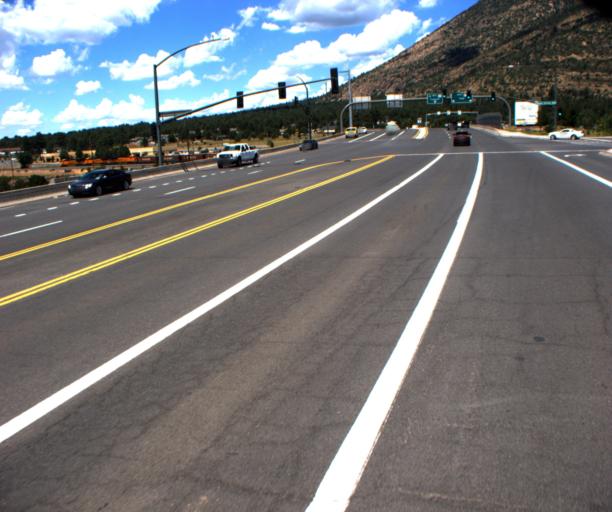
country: US
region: Arizona
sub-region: Coconino County
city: Flagstaff
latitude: 35.2188
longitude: -111.5844
